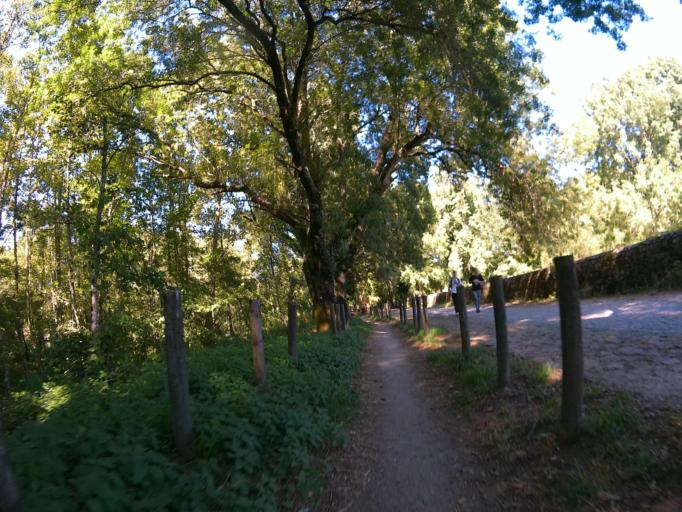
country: PT
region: Viana do Castelo
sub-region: Ponte de Lima
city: Ponte de Lima
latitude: 41.7616
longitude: -8.5938
